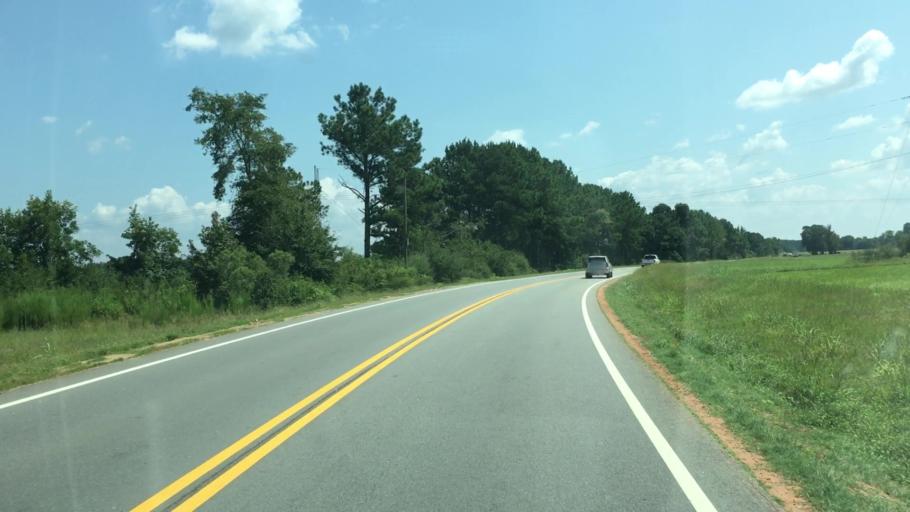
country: US
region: Georgia
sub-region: Oconee County
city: Watkinsville
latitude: 33.8067
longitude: -83.4278
